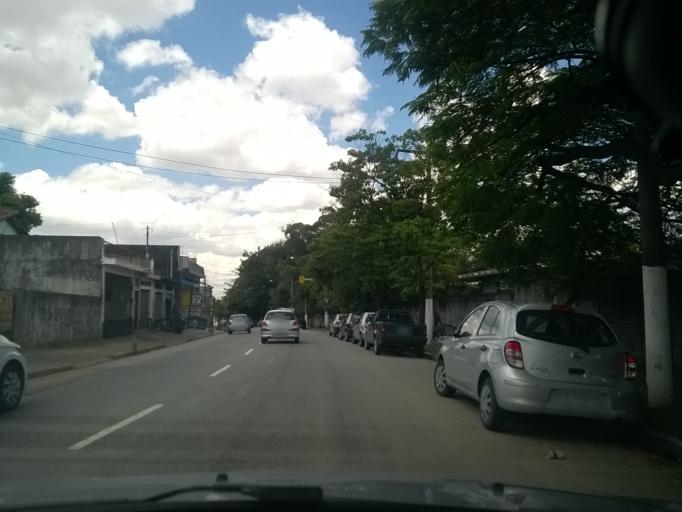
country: BR
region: Sao Paulo
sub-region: Osasco
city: Osasco
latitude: -23.5216
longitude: -46.7788
